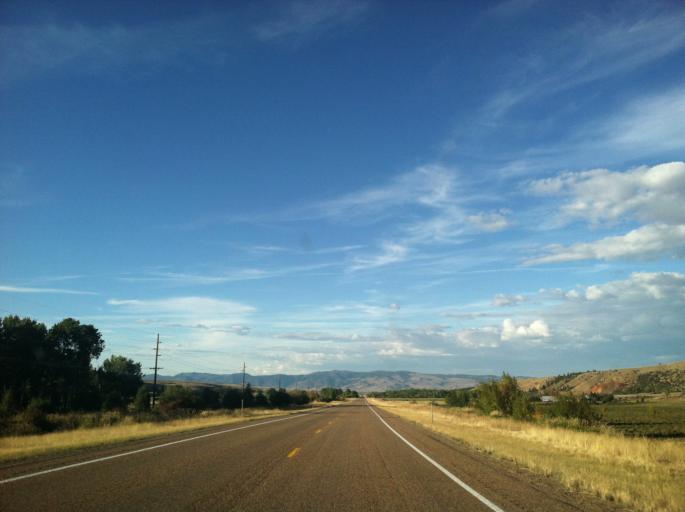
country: US
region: Montana
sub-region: Granite County
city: Philipsburg
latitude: 46.5168
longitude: -113.2272
